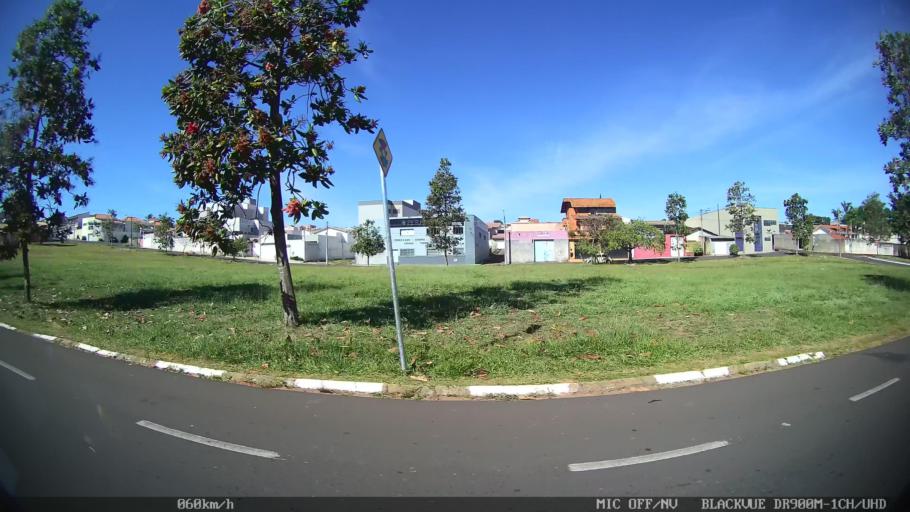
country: BR
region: Sao Paulo
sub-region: Franca
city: Franca
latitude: -20.5210
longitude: -47.3812
